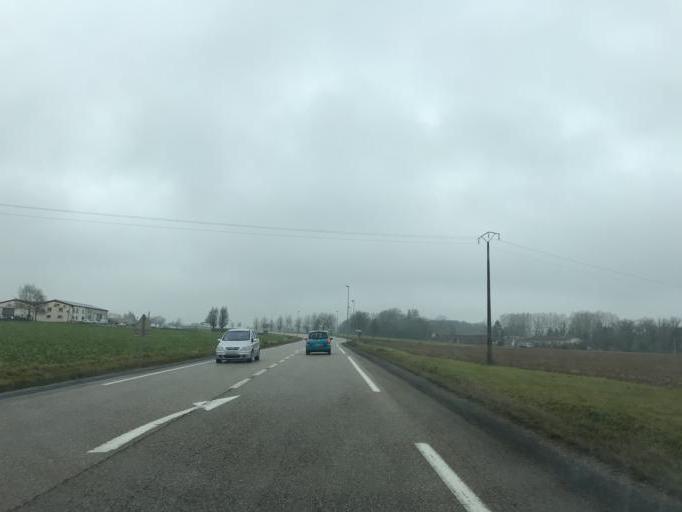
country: FR
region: Rhone-Alpes
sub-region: Departement de l'Ain
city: Peronnas
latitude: 46.1721
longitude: 5.1916
